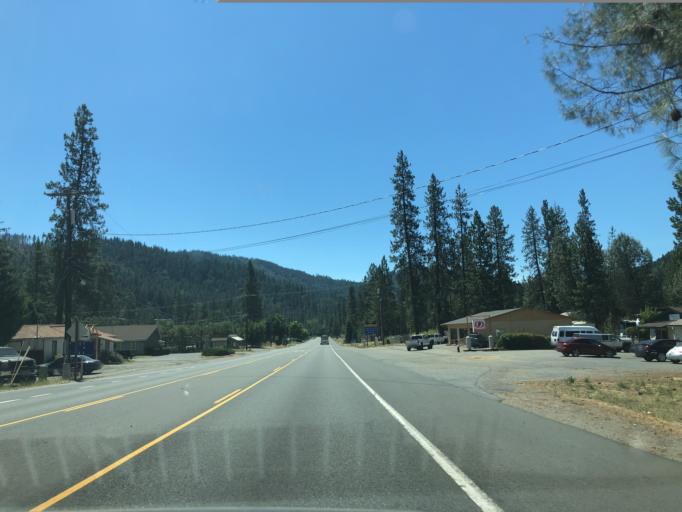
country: US
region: California
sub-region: Trinity County
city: Weaverville
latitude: 40.7200
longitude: -122.9282
